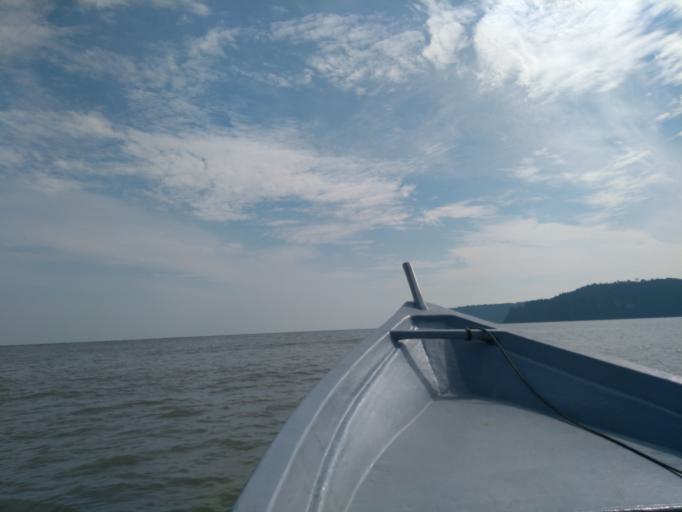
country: MY
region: Sarawak
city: Kuching
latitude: 1.7047
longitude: 110.4304
